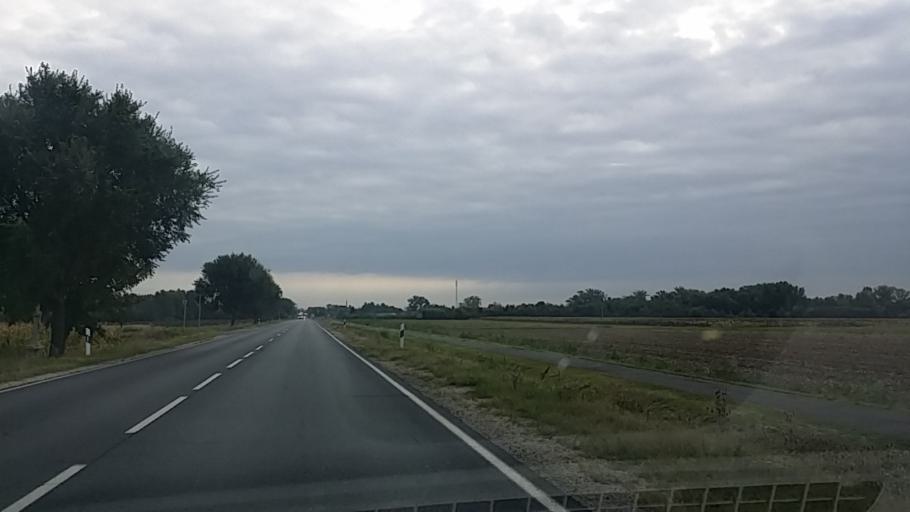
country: HU
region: Gyor-Moson-Sopron
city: Kapuvar
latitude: 47.5893
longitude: 17.0004
